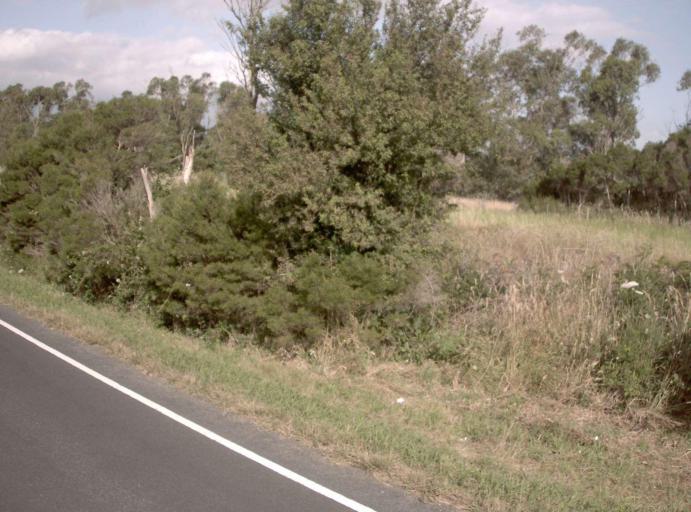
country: AU
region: Victoria
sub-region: Cardinia
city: Bunyip
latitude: -38.1513
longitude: 145.7343
